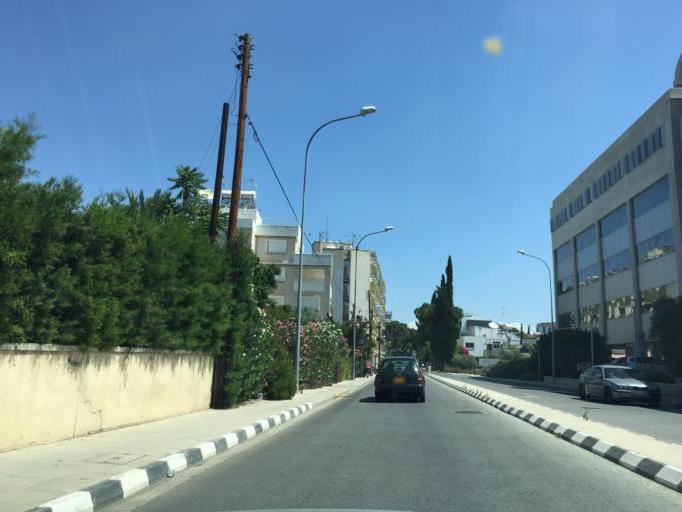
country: CY
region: Lefkosia
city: Nicosia
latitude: 35.1665
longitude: 33.3415
